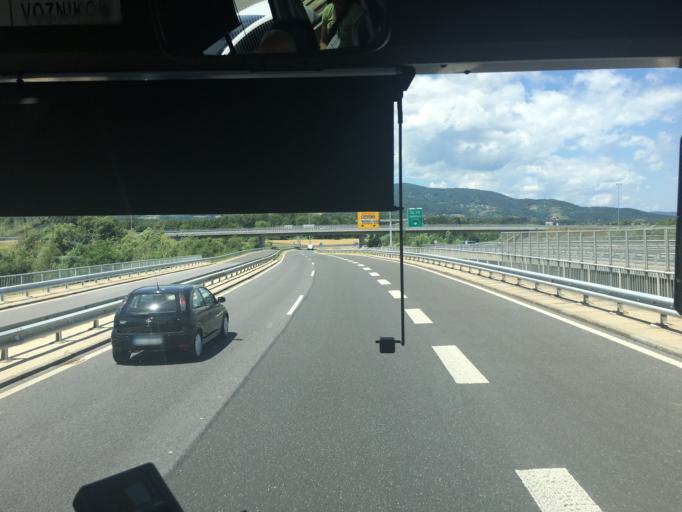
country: SI
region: Hoce-Slivnica
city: Radizel
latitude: 46.4822
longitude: 15.6585
